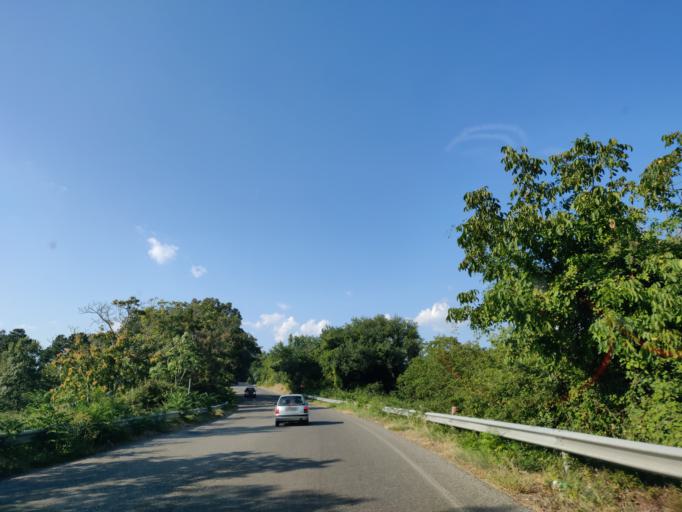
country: IT
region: Latium
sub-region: Provincia di Viterbo
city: Valentano
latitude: 42.5917
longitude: 11.8374
